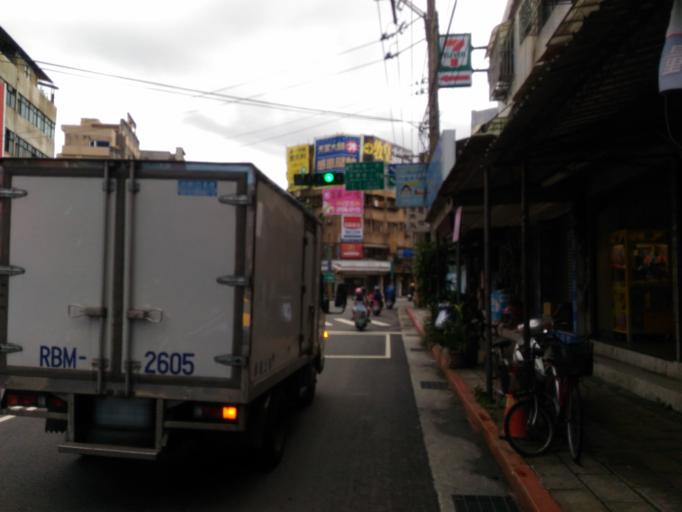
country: TW
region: Taipei
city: Taipei
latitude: 24.9889
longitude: 121.5628
